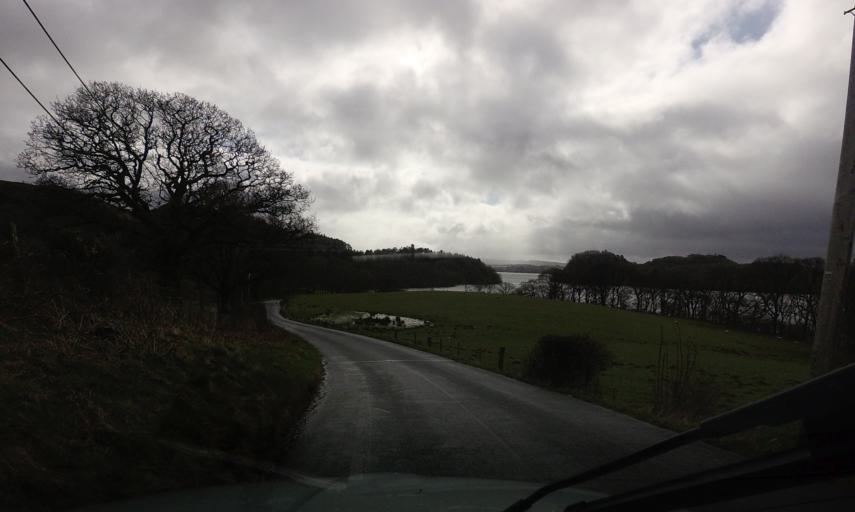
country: GB
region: Scotland
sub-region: West Dunbartonshire
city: Balloch
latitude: 56.0919
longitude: -4.5514
